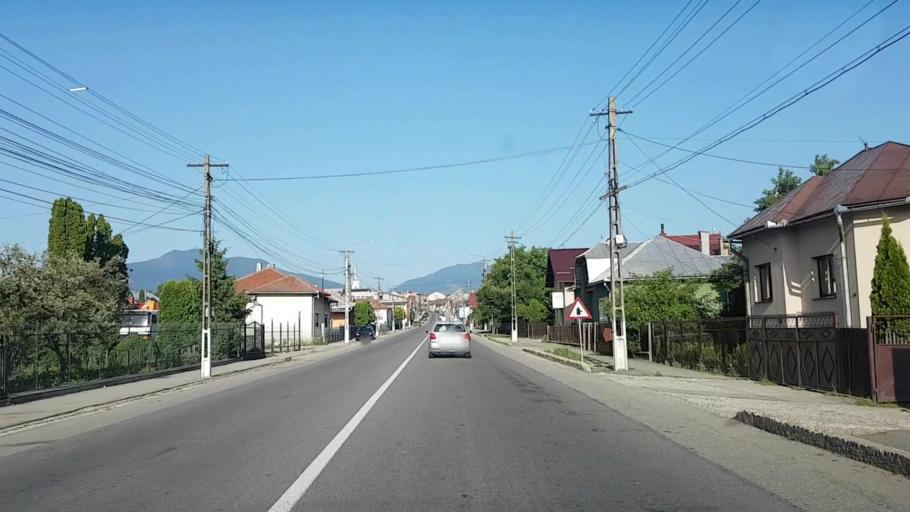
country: RO
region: Bistrita-Nasaud
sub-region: Comuna Prundu Bargaului
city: Susenii Bargaului
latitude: 47.2200
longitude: 24.7323
